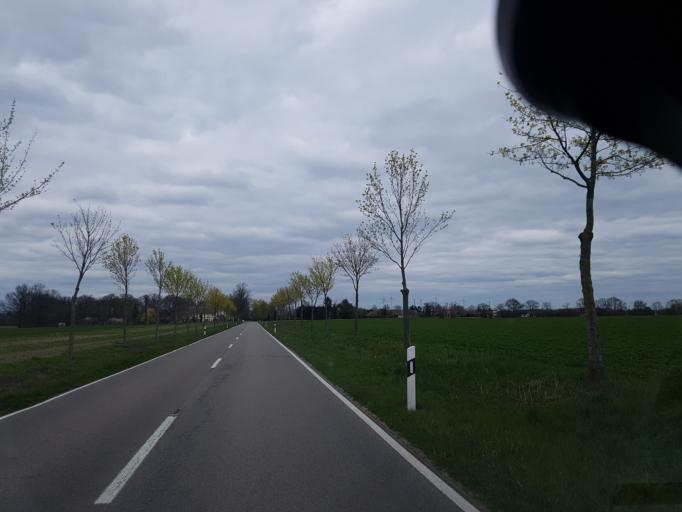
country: DE
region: Brandenburg
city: Juterbog
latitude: 51.9268
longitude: 13.1151
